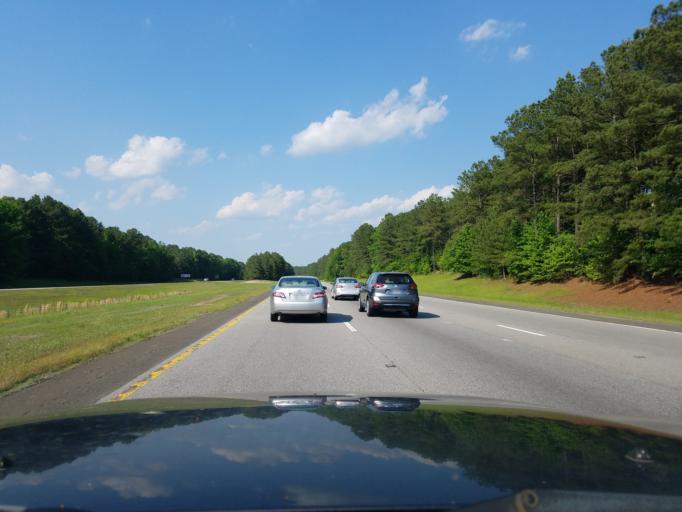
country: US
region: North Carolina
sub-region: Granville County
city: Butner
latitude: 36.1506
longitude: -78.7219
